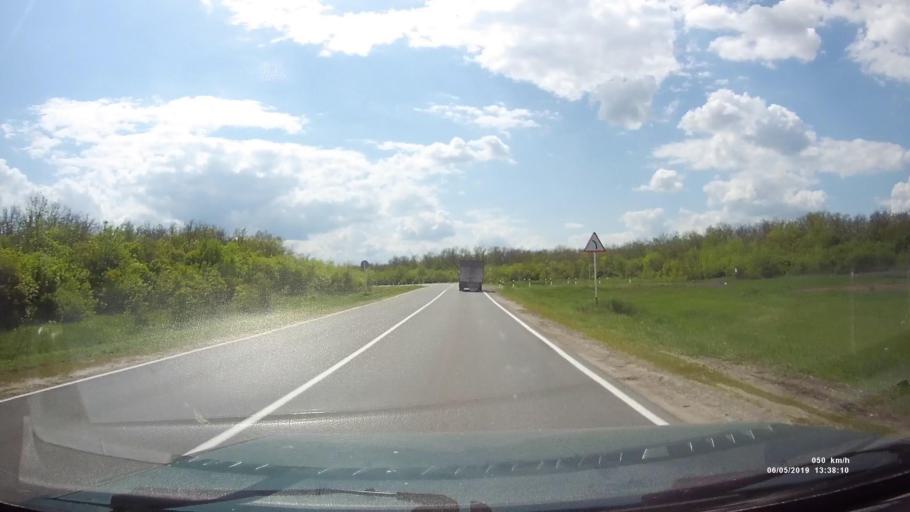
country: RU
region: Rostov
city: Ust'-Donetskiy
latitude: 47.6878
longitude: 40.7120
